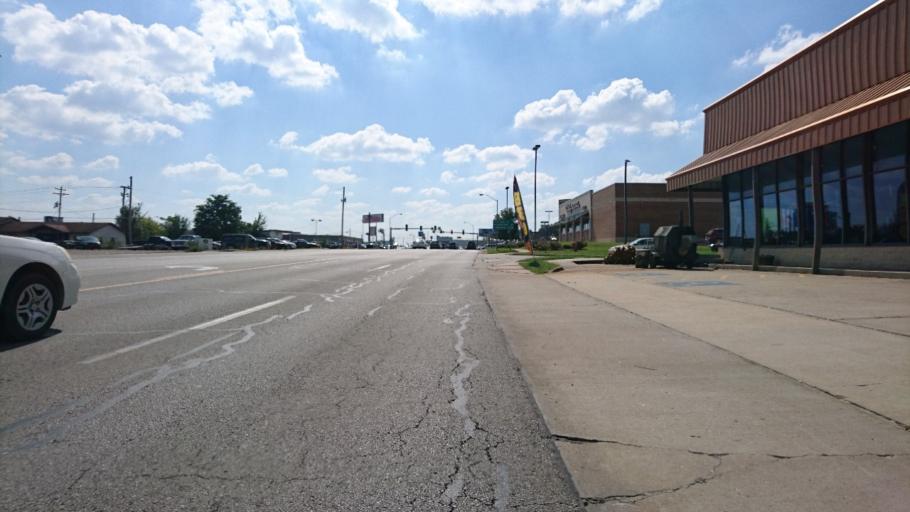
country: US
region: Missouri
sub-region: Laclede County
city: Lebanon
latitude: 37.6775
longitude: -92.6571
